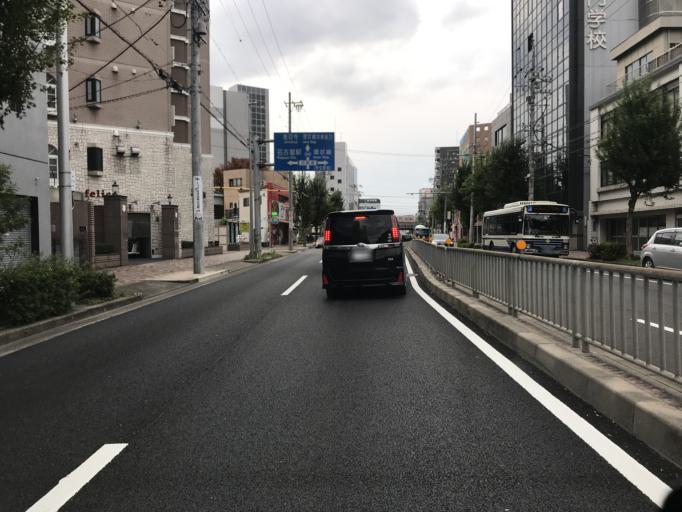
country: JP
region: Aichi
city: Nagoya-shi
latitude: 35.1775
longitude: 136.8810
